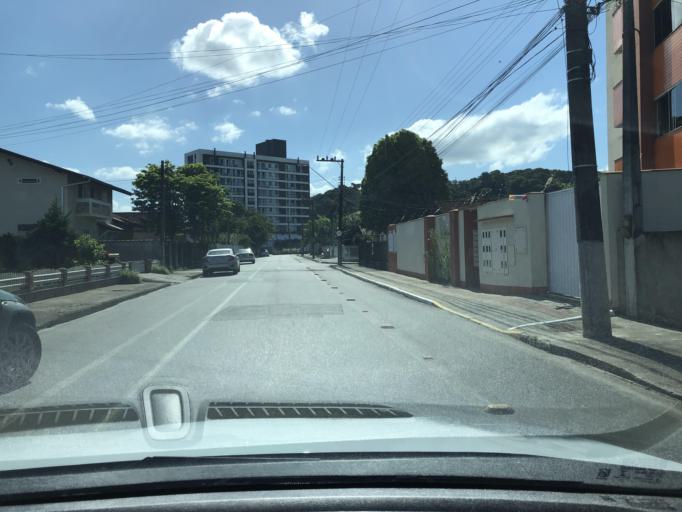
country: BR
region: Santa Catarina
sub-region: Joinville
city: Joinville
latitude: -26.2688
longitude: -48.8475
